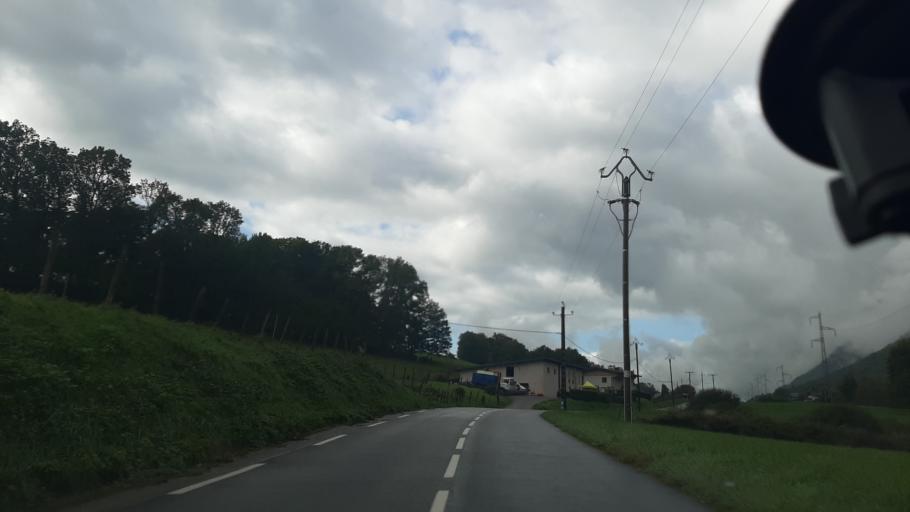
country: FR
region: Rhone-Alpes
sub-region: Departement de la Savoie
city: Gresy-sur-Isere
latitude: 45.6116
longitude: 6.2739
